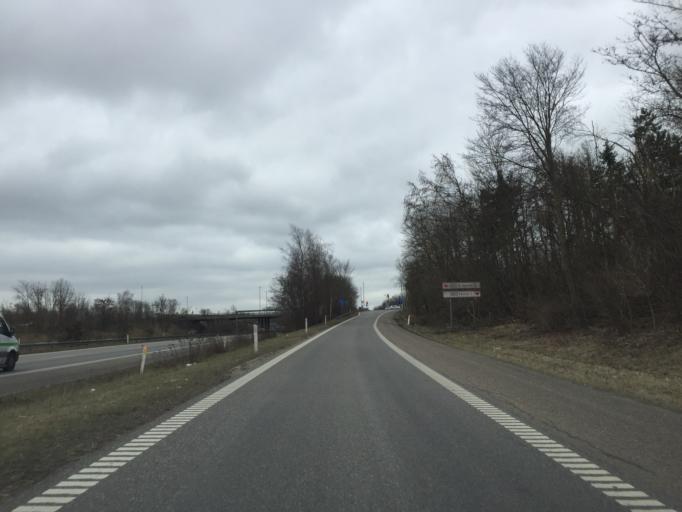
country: DK
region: Capital Region
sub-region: Fureso Kommune
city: Farum
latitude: 55.8260
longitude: 12.3780
